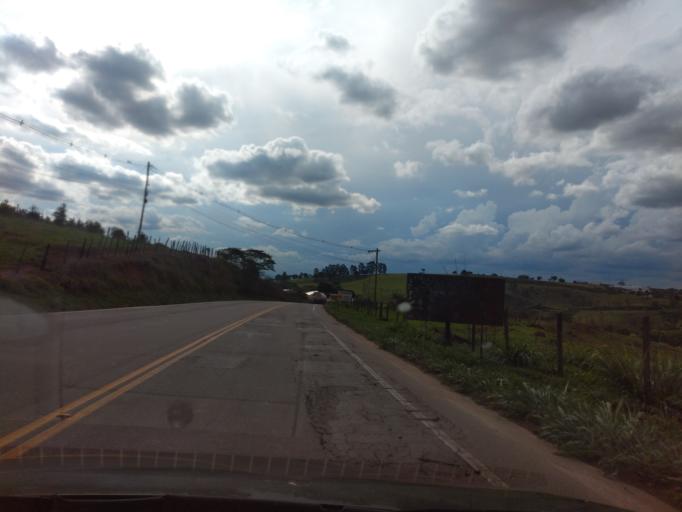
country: BR
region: Minas Gerais
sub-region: Varginha
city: Varginha
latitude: -21.6142
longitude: -45.4232
